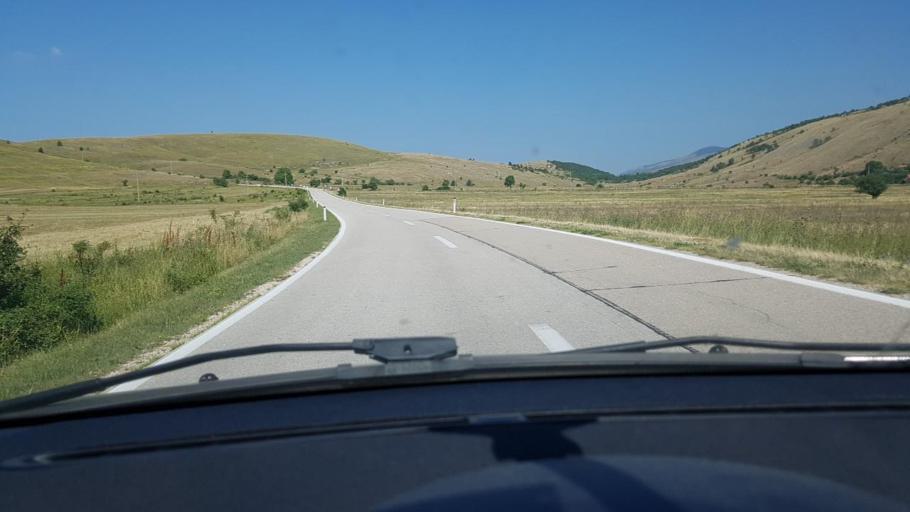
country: BA
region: Federation of Bosnia and Herzegovina
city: Bosansko Grahovo
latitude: 44.1305
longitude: 16.5120
